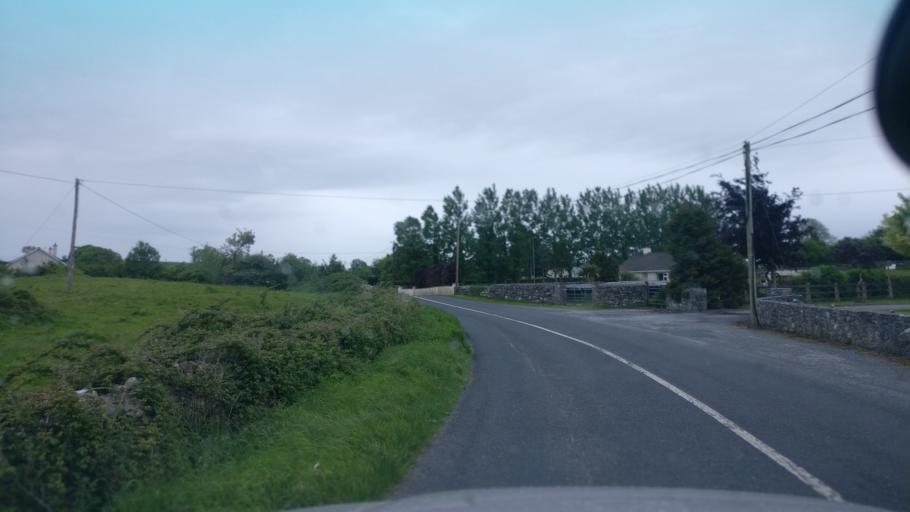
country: IE
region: Connaught
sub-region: County Galway
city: Gort
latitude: 53.0629
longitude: -8.7663
